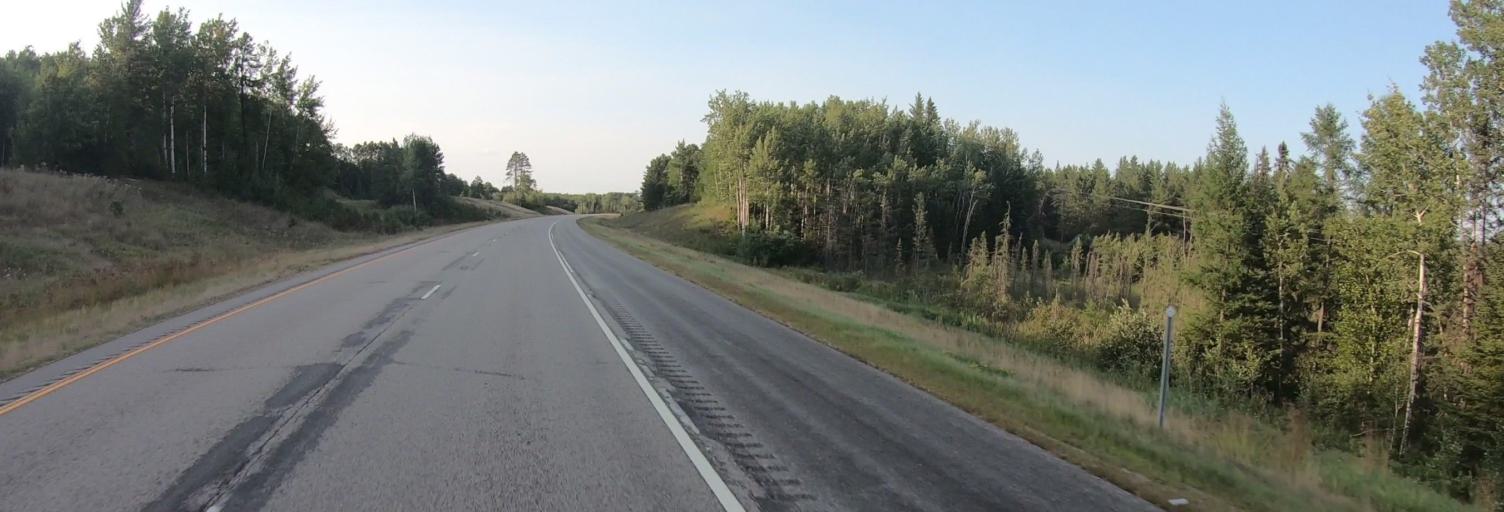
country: US
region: Minnesota
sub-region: Saint Louis County
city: Mountain Iron
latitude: 47.6828
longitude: -92.6385
